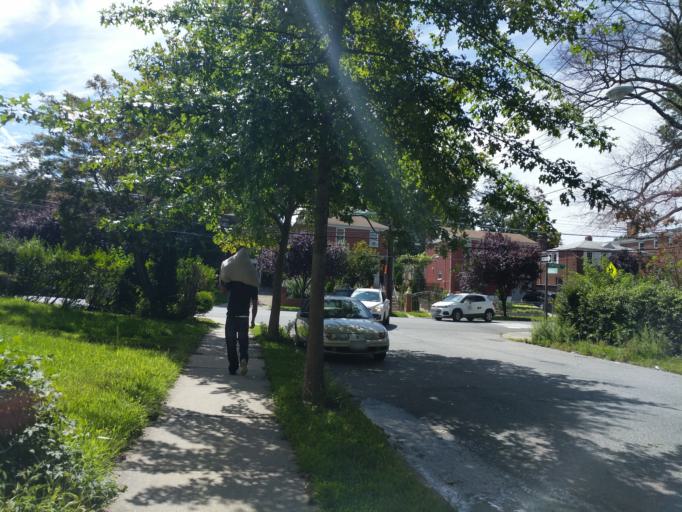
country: US
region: New Jersey
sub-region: Hudson County
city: Bayonne
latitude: 40.6197
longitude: -74.0761
